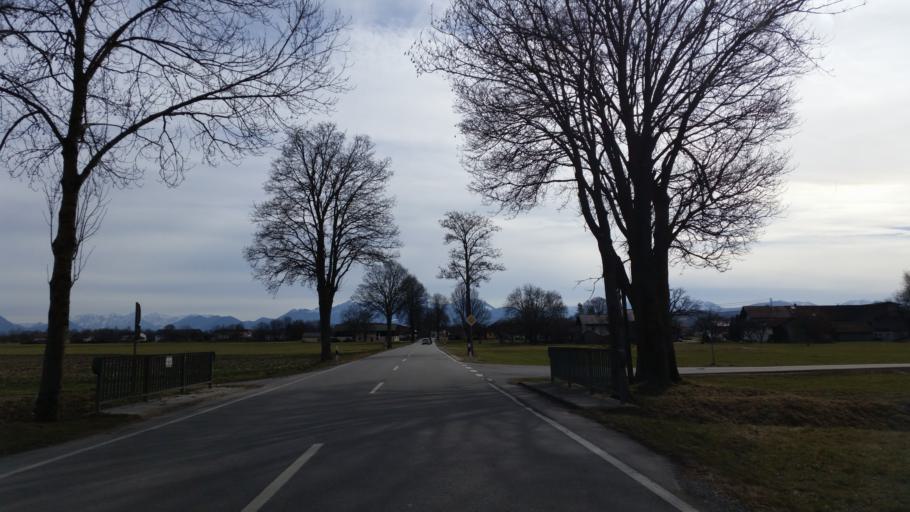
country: DE
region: Bavaria
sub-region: Upper Bavaria
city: Bruckmuhl
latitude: 47.8973
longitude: 11.9254
